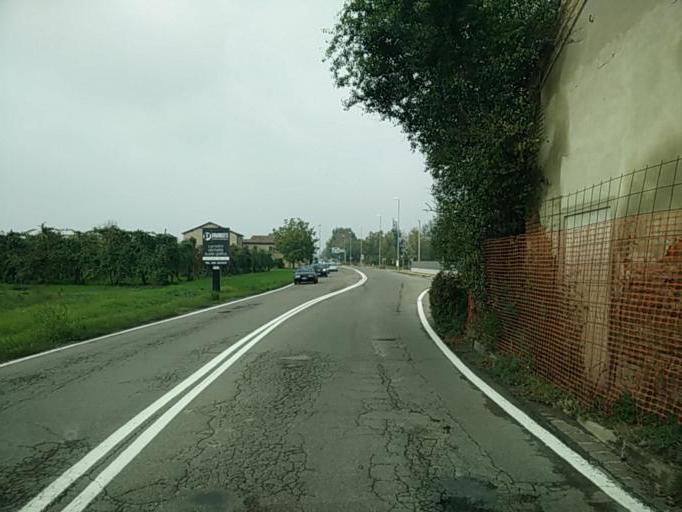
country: IT
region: Emilia-Romagna
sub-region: Provincia di Modena
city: Carpi Centro
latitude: 44.7817
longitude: 10.8646
